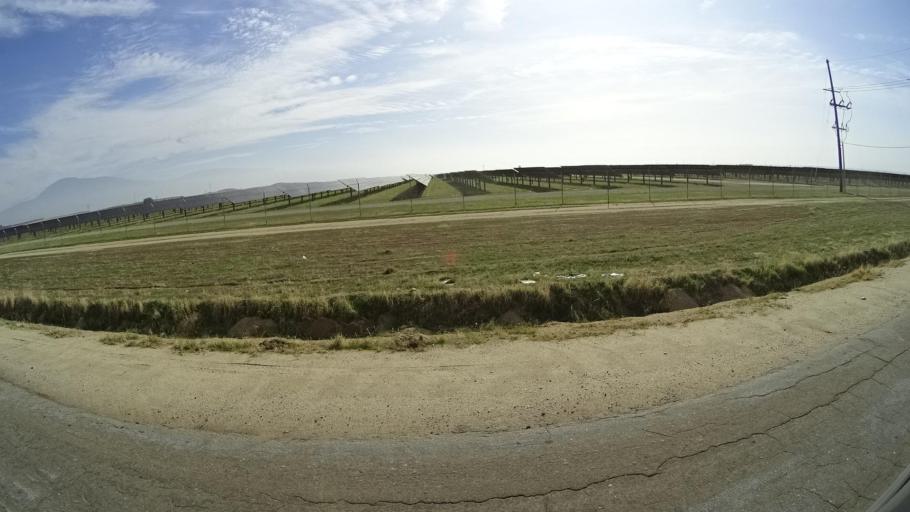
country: US
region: California
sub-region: Kern County
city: Arvin
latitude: 35.3257
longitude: -118.8138
